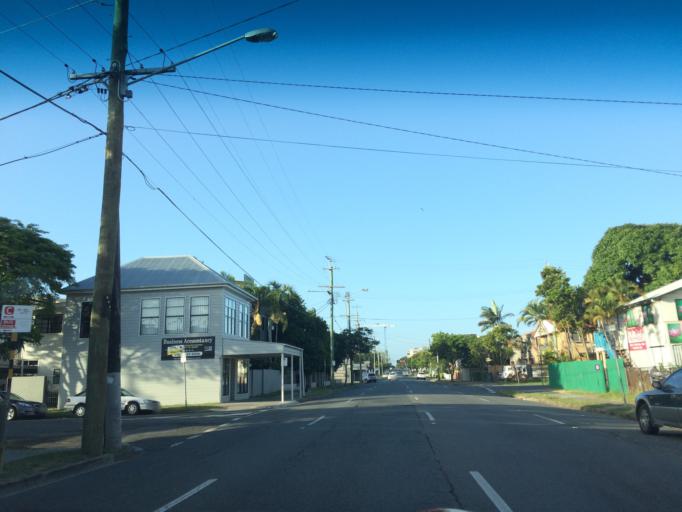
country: AU
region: Queensland
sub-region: Brisbane
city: Woolloongabba
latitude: -27.4846
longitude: 153.0403
